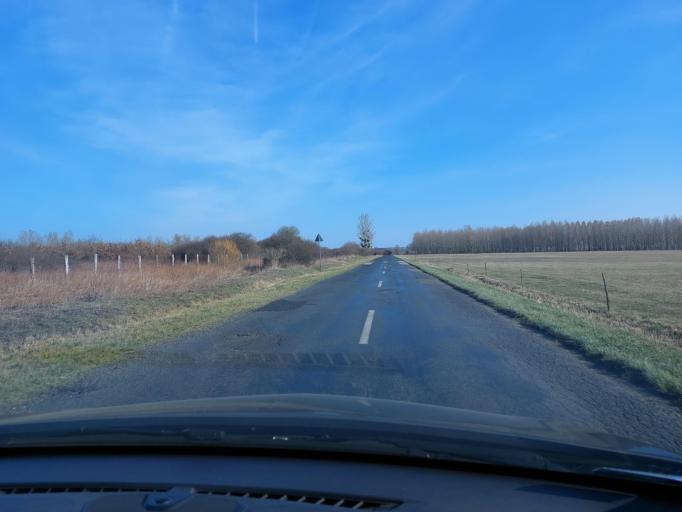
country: HU
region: Veszprem
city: Devecser
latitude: 47.1290
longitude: 17.4032
